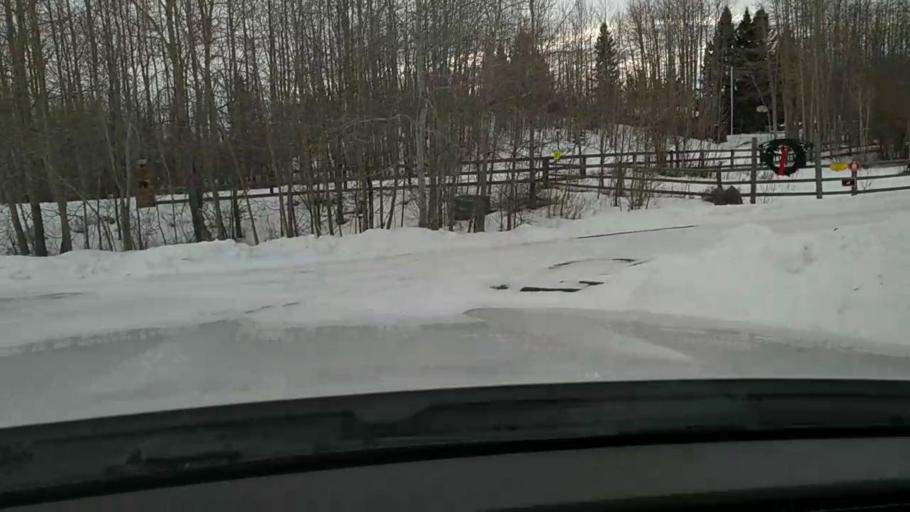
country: CA
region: Alberta
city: Cochrane
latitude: 51.2001
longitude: -114.2894
